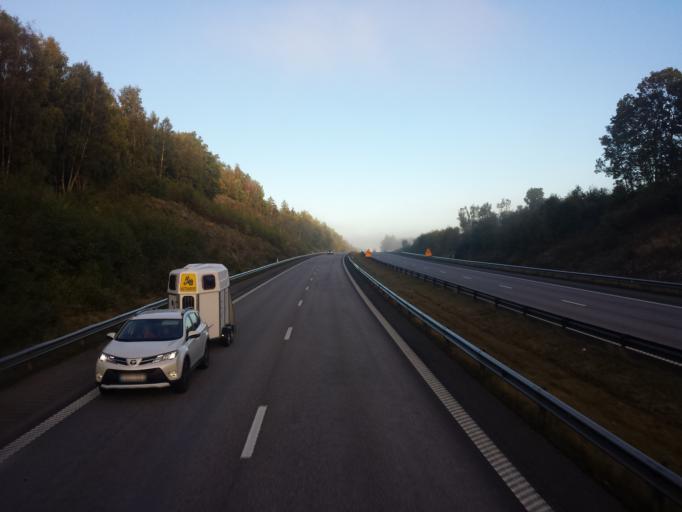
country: SE
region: Halland
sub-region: Kungsbacka Kommun
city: Fjaeras kyrkby
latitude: 57.4398
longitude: 12.1221
